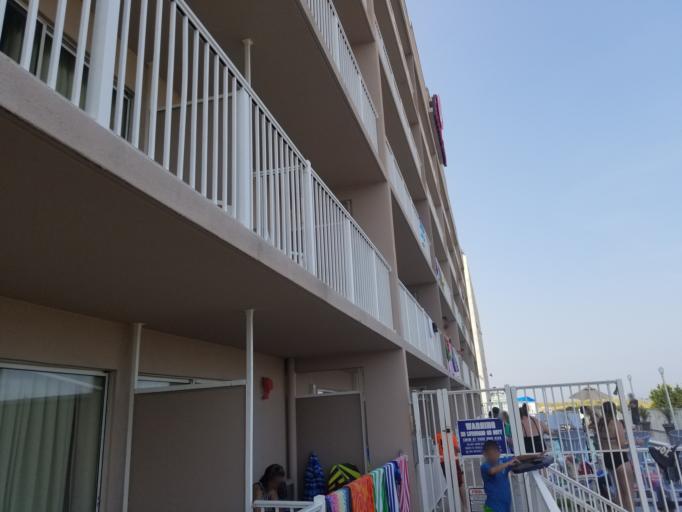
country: US
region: Maryland
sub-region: Worcester County
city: Ocean City
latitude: 38.3579
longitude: -75.0725
